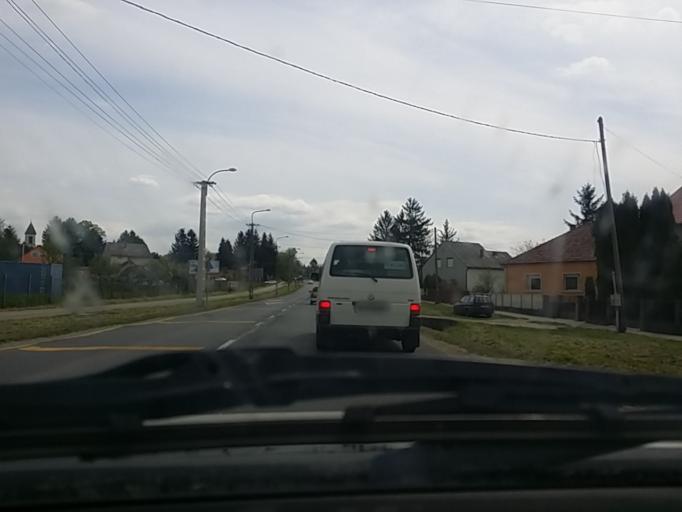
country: HU
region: Zala
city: Nagykanizsa
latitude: 46.4503
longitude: 17.0202
